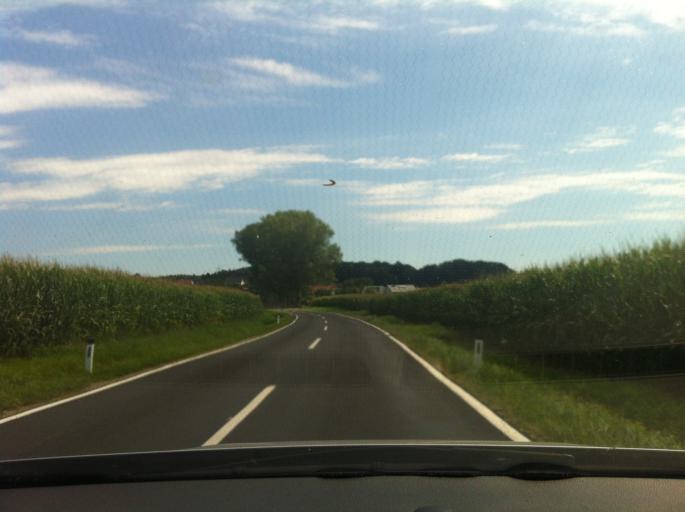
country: AT
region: Styria
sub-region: Politischer Bezirk Hartberg-Fuerstenfeld
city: Blaindorf
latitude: 47.1625
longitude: 15.8724
